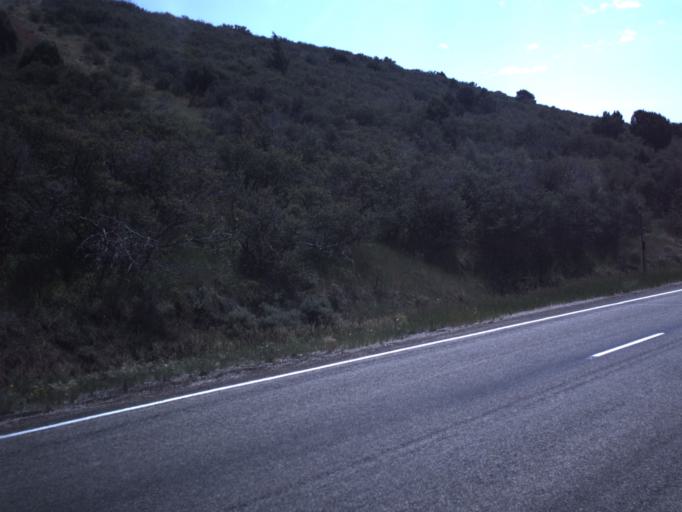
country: US
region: Utah
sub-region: Uintah County
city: Vernal
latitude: 40.6683
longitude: -109.4824
